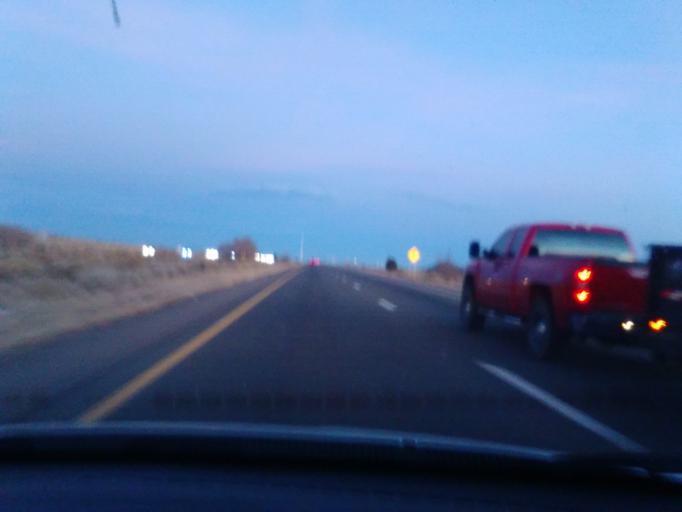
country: US
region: New Mexico
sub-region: Santa Fe County
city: La Cienega
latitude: 35.5211
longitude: -106.1792
